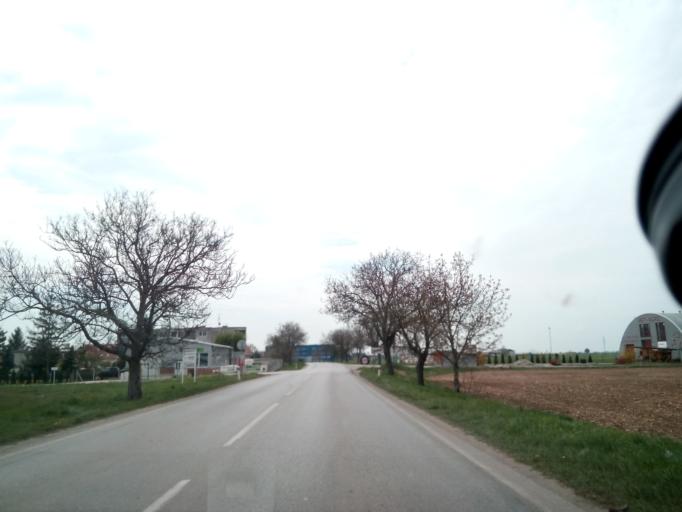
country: SK
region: Trnavsky
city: Vrbove
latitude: 48.6021
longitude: 17.7488
